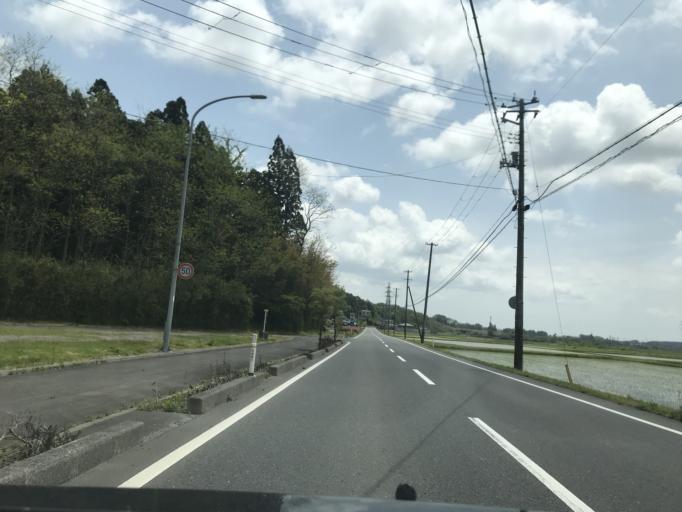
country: JP
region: Miyagi
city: Furukawa
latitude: 38.6692
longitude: 140.9960
